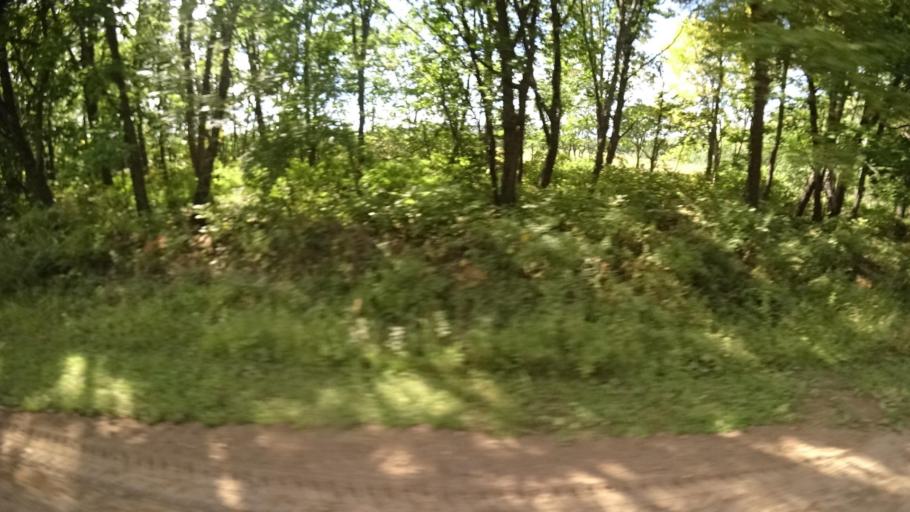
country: RU
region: Primorskiy
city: Yakovlevka
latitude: 44.4151
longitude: 133.5703
